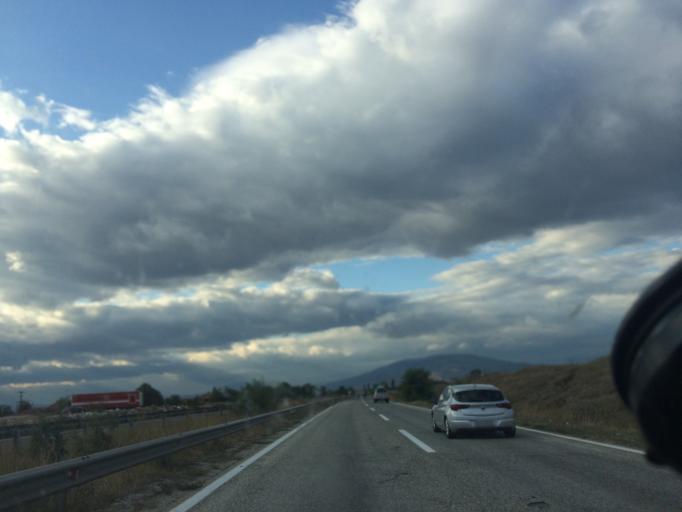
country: MK
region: Petrovec
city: Petrovec
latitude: 41.9206
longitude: 21.6367
